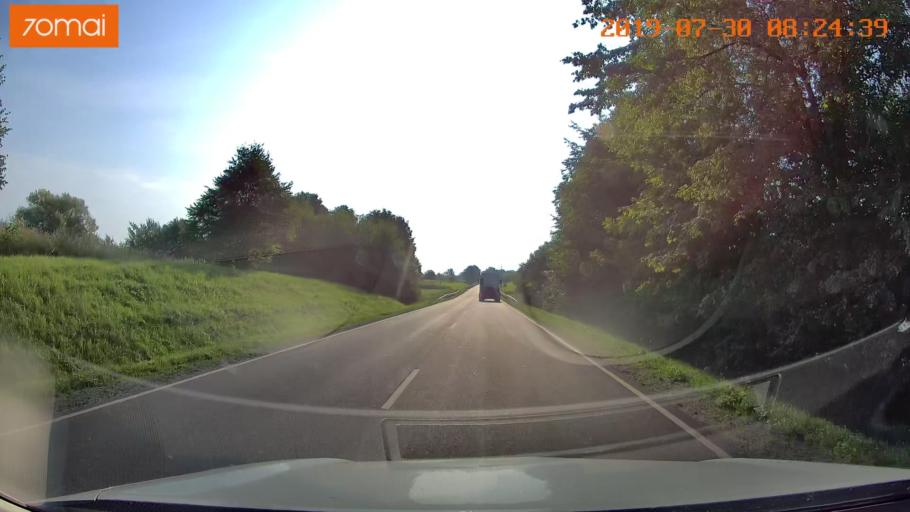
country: RU
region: Kaliningrad
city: Chernyakhovsk
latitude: 54.6239
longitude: 21.5627
